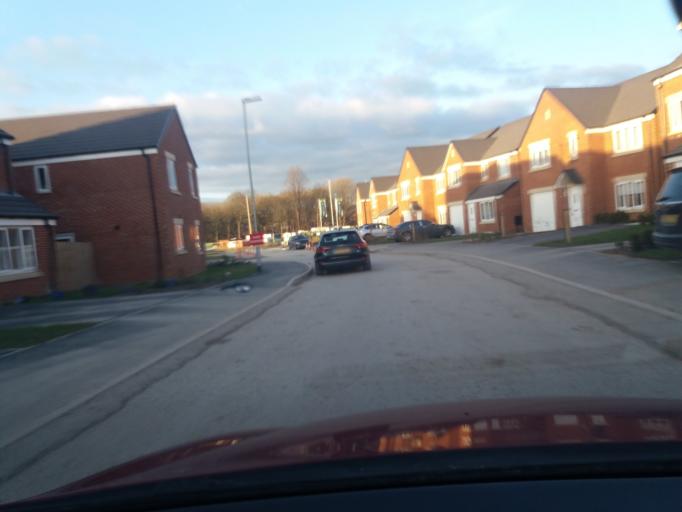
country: GB
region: England
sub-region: Lancashire
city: Euxton
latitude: 53.6760
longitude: -2.6728
